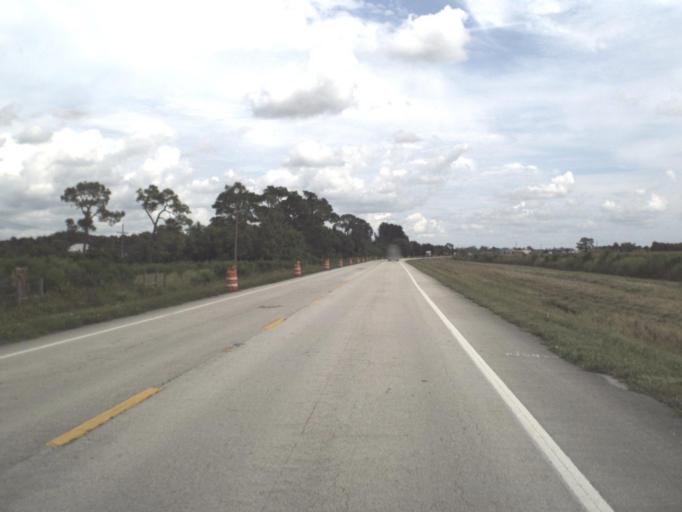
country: US
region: Florida
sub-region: Okeechobee County
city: Taylor Creek
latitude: 27.2854
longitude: -80.7055
